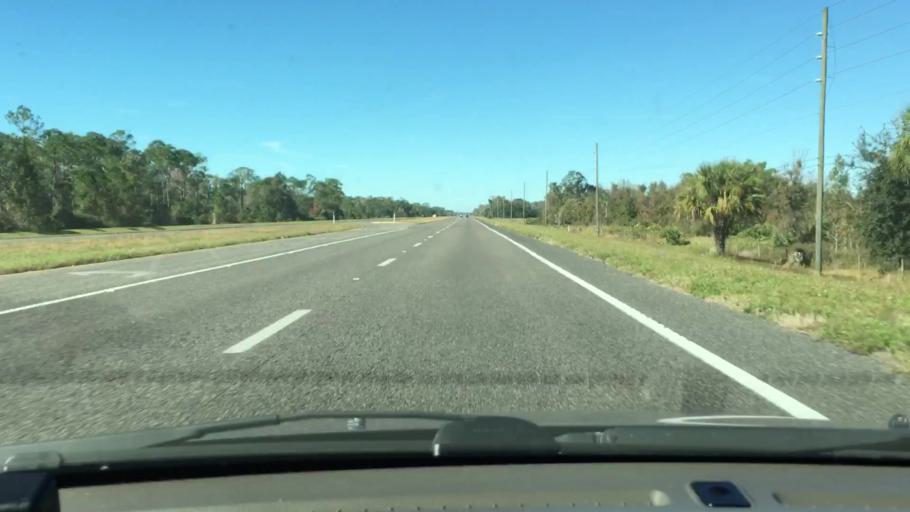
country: US
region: Florida
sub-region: Brevard County
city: June Park
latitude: 28.1197
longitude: -80.9435
